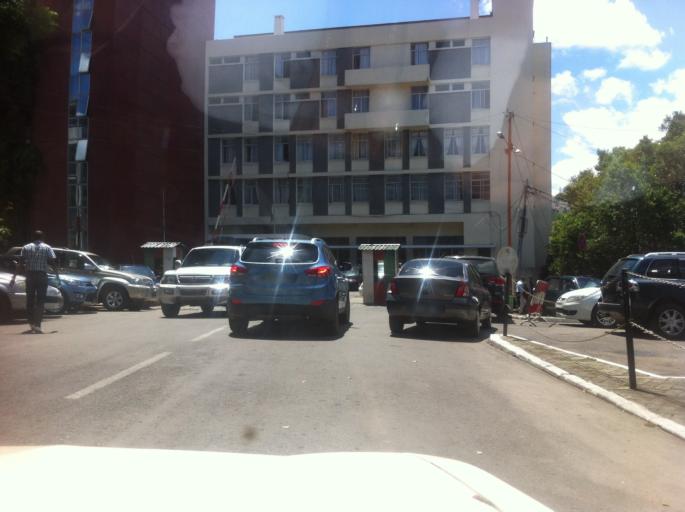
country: MG
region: Analamanga
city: Antananarivo
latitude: -18.9108
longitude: 47.5236
